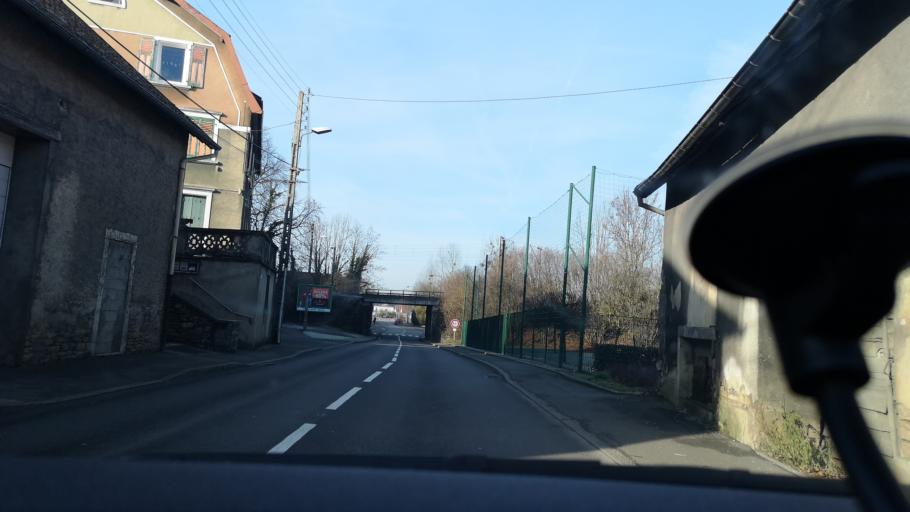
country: FR
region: Franche-Comte
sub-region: Departement du Doubs
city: Voujeaucourt
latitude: 47.4745
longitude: 6.7641
